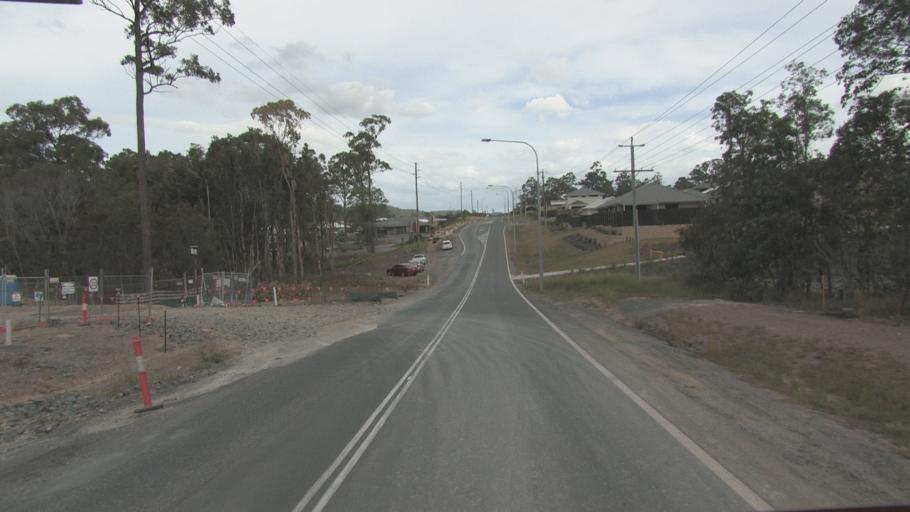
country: AU
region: Queensland
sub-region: Logan
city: Windaroo
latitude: -27.7276
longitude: 153.1638
